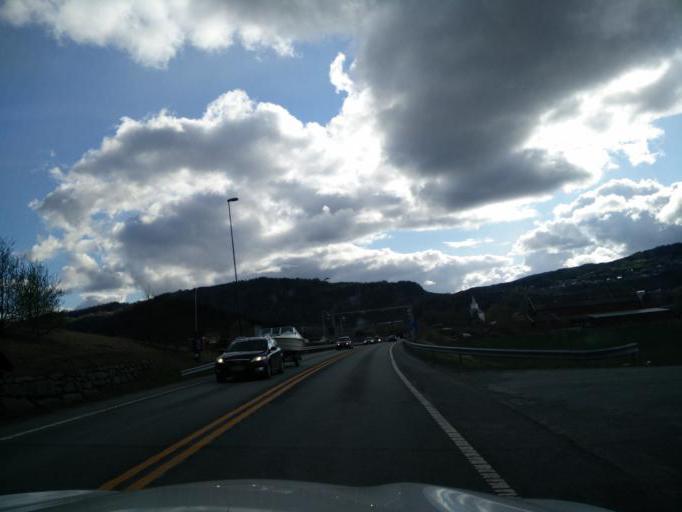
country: NO
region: Sor-Trondelag
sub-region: Melhus
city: Melhus
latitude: 63.3217
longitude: 10.2080
